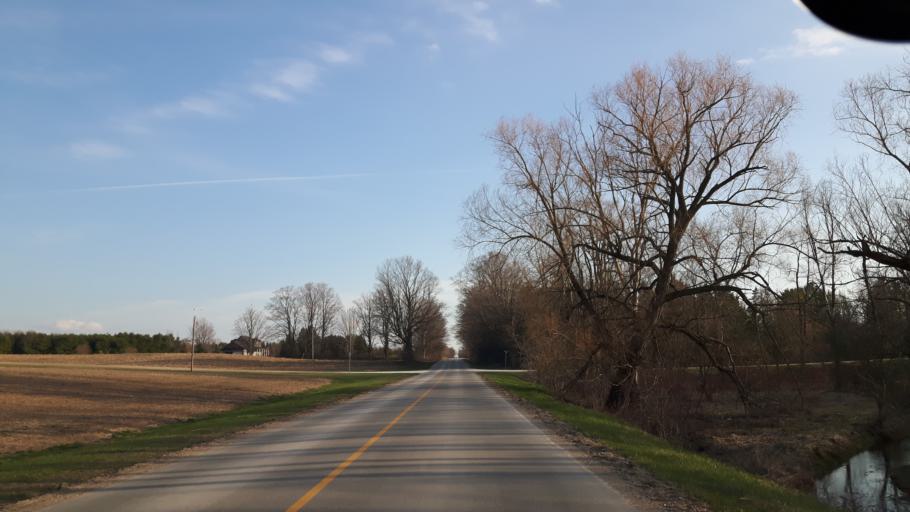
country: CA
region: Ontario
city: Goderich
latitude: 43.6809
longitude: -81.6644
